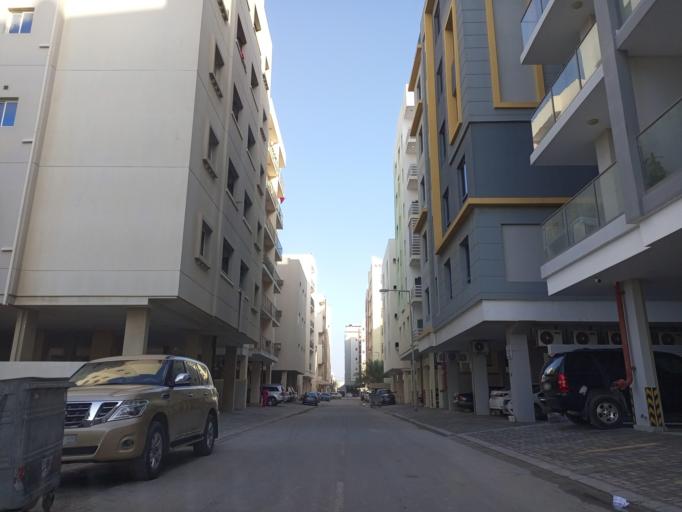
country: BH
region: Muharraq
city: Al Hadd
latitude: 26.2336
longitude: 50.6457
